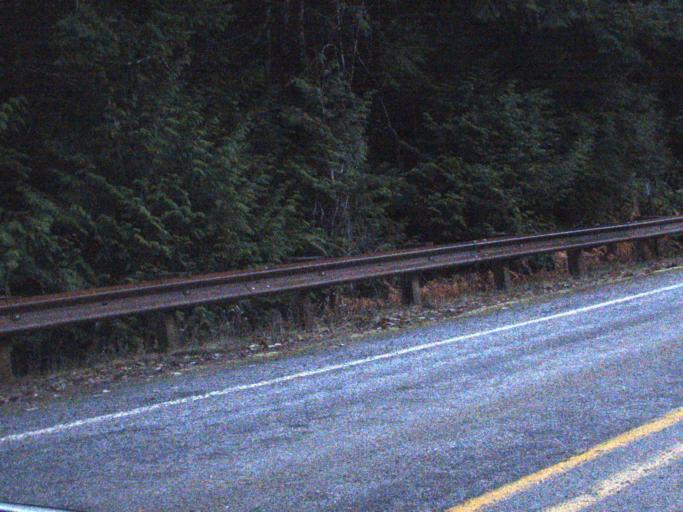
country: US
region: Washington
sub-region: Snohomish County
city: Darrington
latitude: 48.7080
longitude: -121.1388
